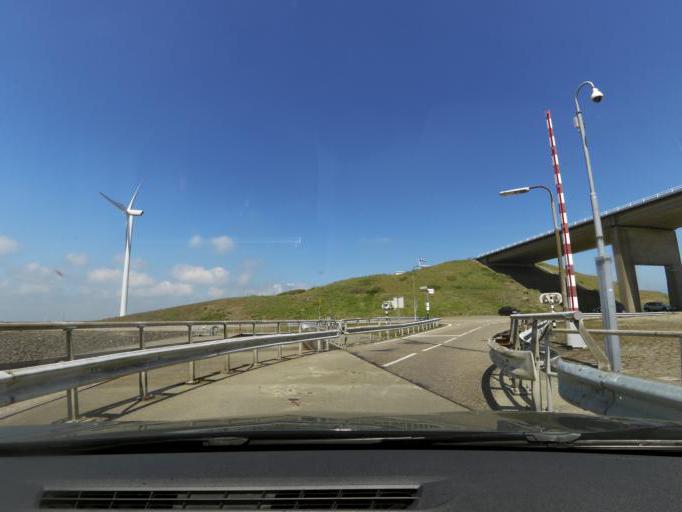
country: NL
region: Zeeland
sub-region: Gemeente Noord-Beveland
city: Kamperland
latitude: 51.6187
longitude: 3.6839
